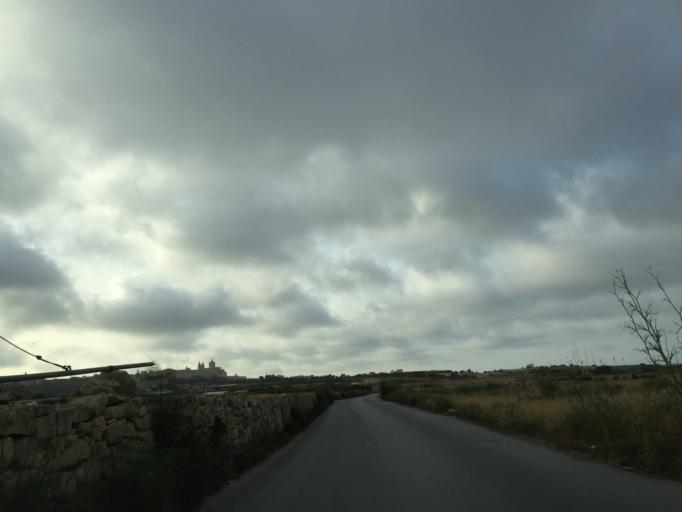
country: MT
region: Ir-Rabat
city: Rabat
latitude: 35.8738
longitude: 14.4140
